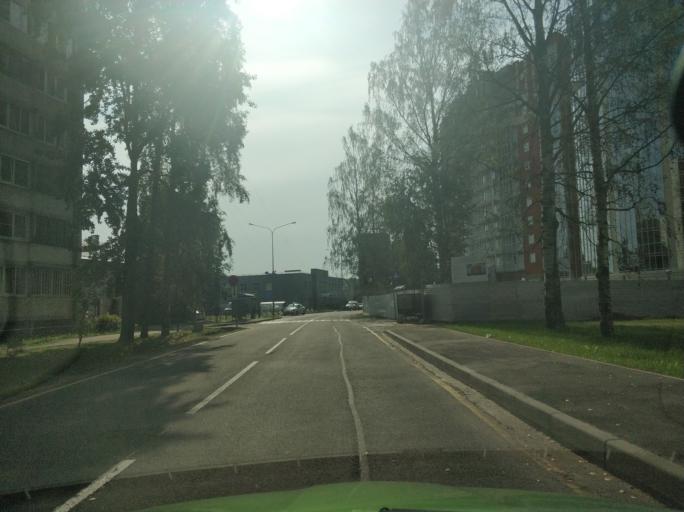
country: RU
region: Leningrad
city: Murino
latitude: 60.0423
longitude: 30.4644
